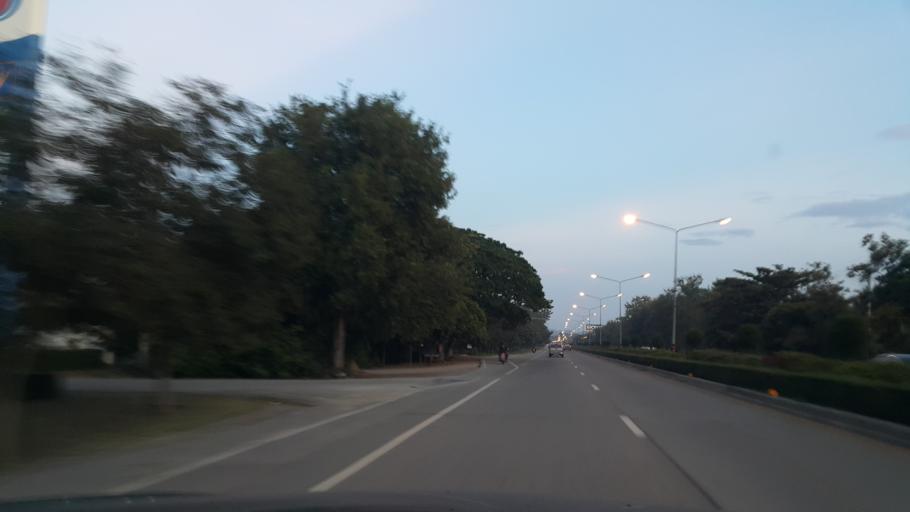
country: TH
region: Lamphun
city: Lamphun
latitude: 18.5670
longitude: 99.0270
